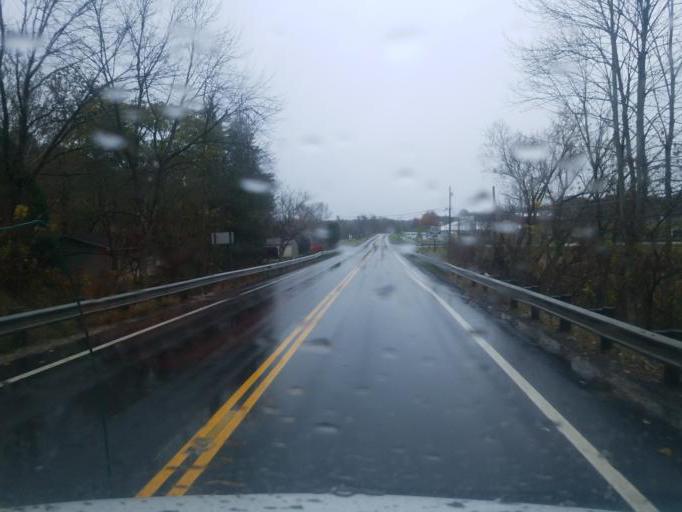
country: US
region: Ohio
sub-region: Washington County
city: Beverly
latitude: 39.4647
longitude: -81.6356
